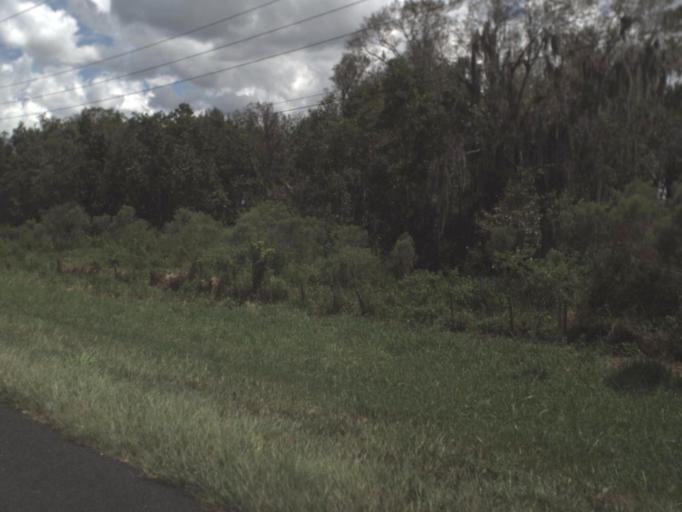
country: US
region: Florida
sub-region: Polk County
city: Lake Wales
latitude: 27.9009
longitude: -81.6378
